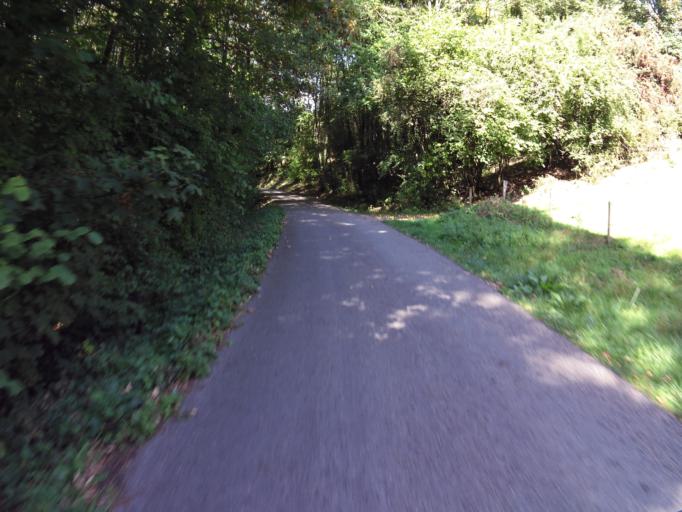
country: DE
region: Rheinland-Pfalz
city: Menningen
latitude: 49.8363
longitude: 6.4787
